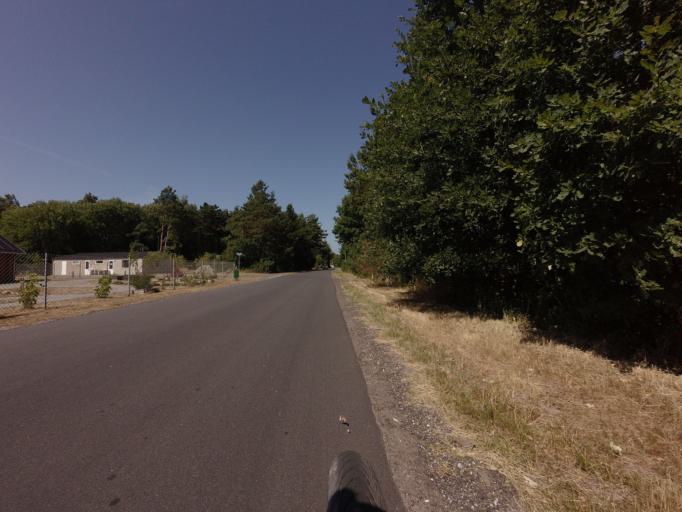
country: DK
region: North Denmark
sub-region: Laeso Kommune
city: Byrum
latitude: 57.2590
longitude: 10.9998
